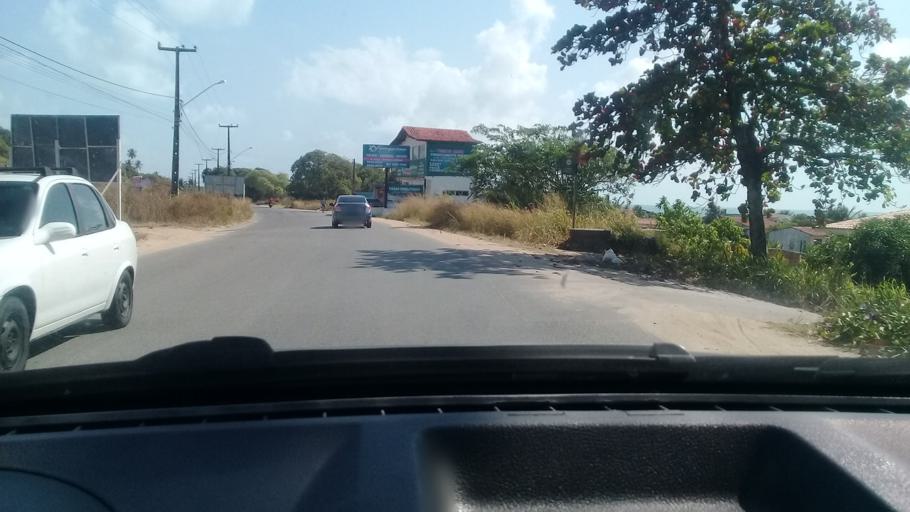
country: BR
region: Pernambuco
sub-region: Itamaraca
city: Itamaraca
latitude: -7.7826
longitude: -34.8373
